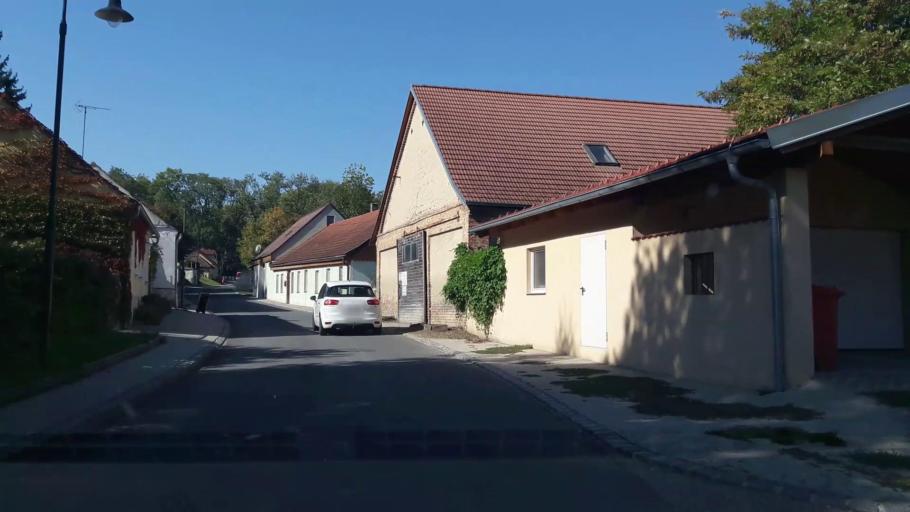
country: AT
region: Lower Austria
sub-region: Politischer Bezirk Korneuburg
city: Ernstbrunn
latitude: 48.5420
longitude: 16.3518
